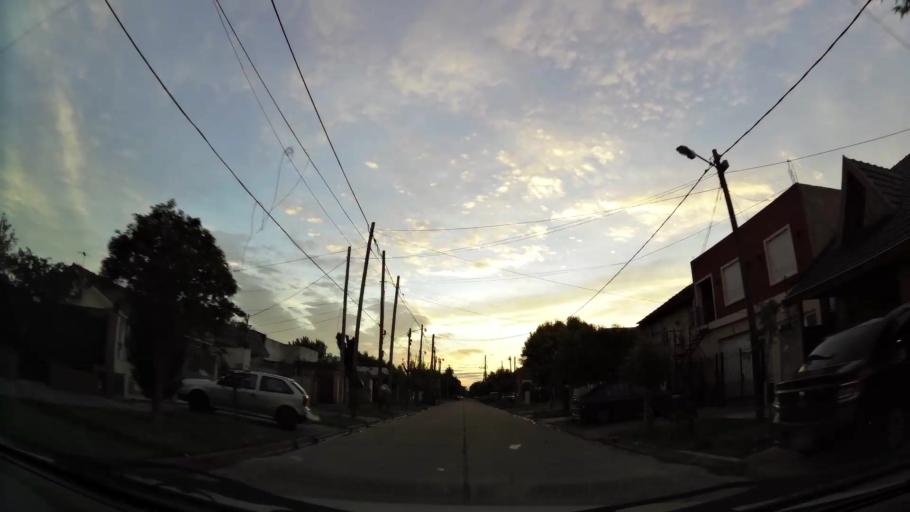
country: AR
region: Buenos Aires
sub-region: Partido de Lomas de Zamora
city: Lomas de Zamora
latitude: -34.7634
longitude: -58.3738
